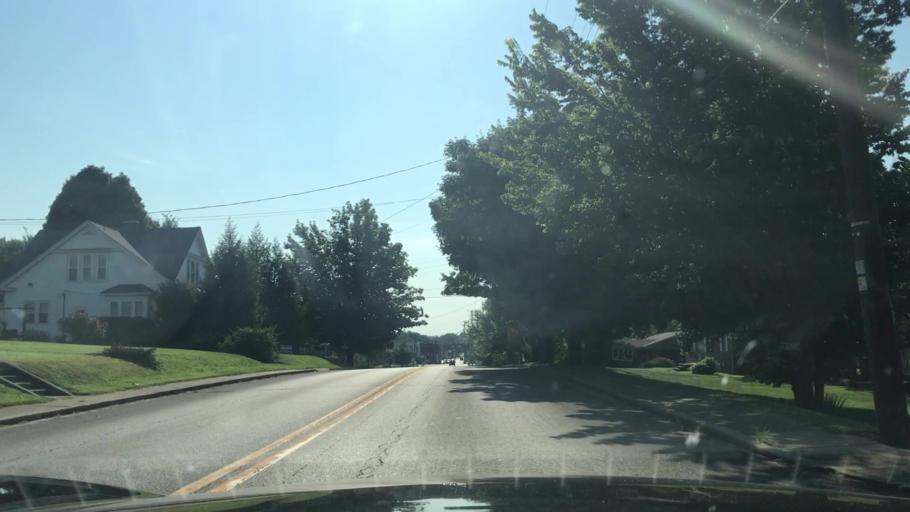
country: US
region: Kentucky
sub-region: Hart County
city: Horse Cave
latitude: 37.1798
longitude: -85.9106
